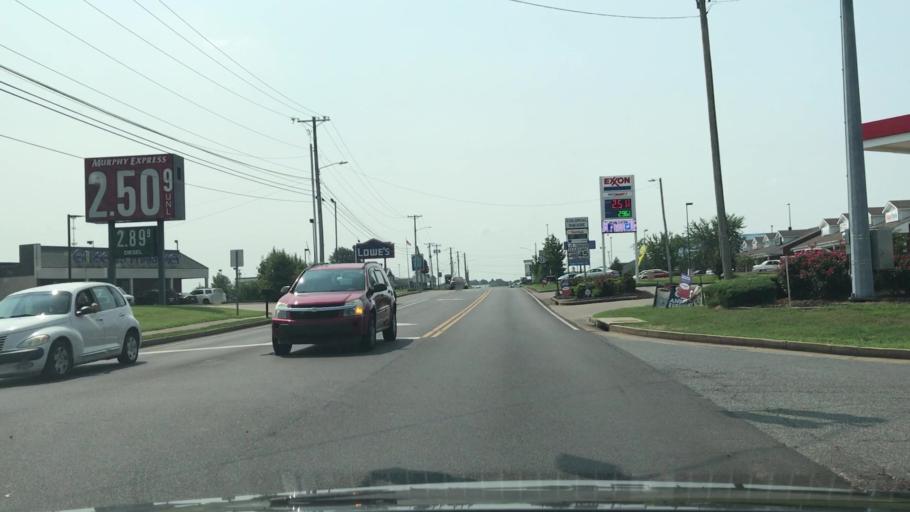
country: US
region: Kentucky
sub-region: Graves County
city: Mayfield
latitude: 36.7226
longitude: -88.6273
